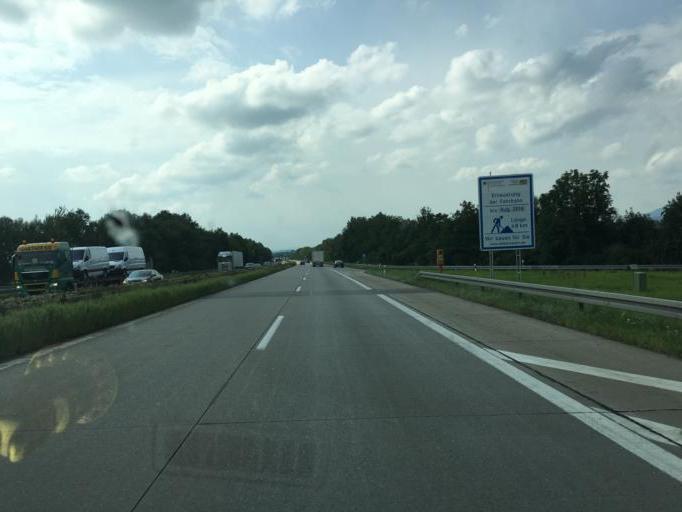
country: DE
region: Bavaria
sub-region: Lower Bavaria
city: Metten
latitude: 48.8468
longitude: 12.8890
